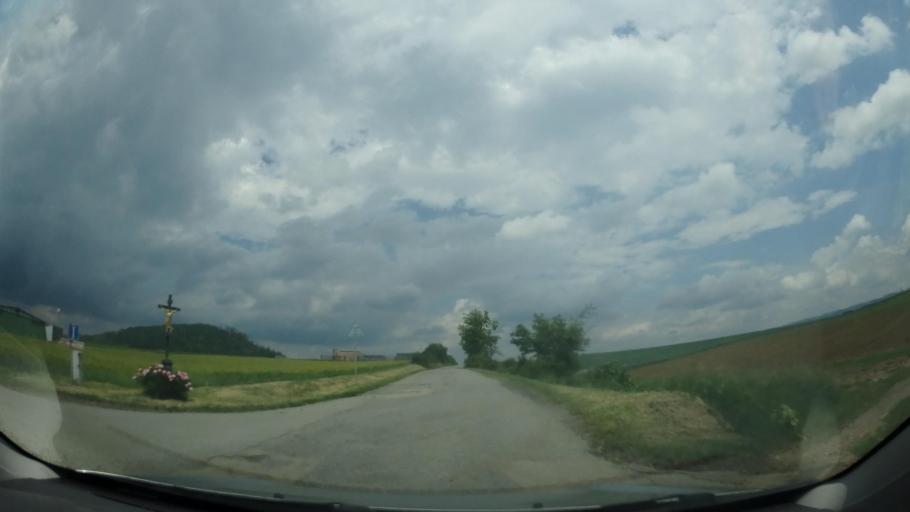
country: CZ
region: South Moravian
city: Boritov
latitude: 49.4312
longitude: 16.5926
